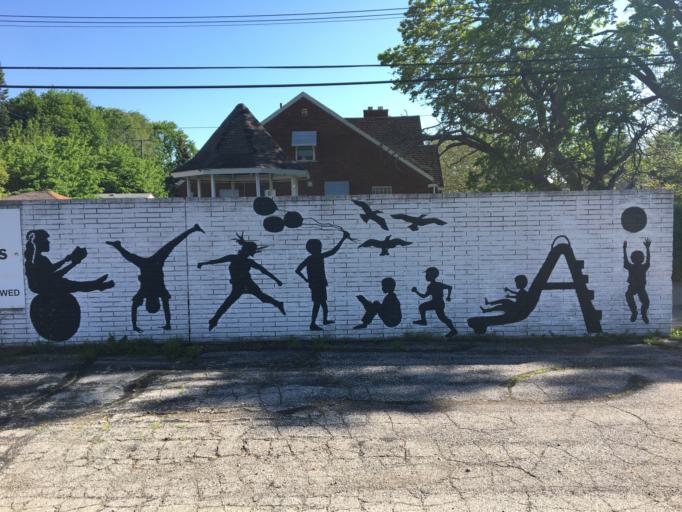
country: US
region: Michigan
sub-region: Wayne County
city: Harper Woods
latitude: 42.4257
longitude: -82.9479
